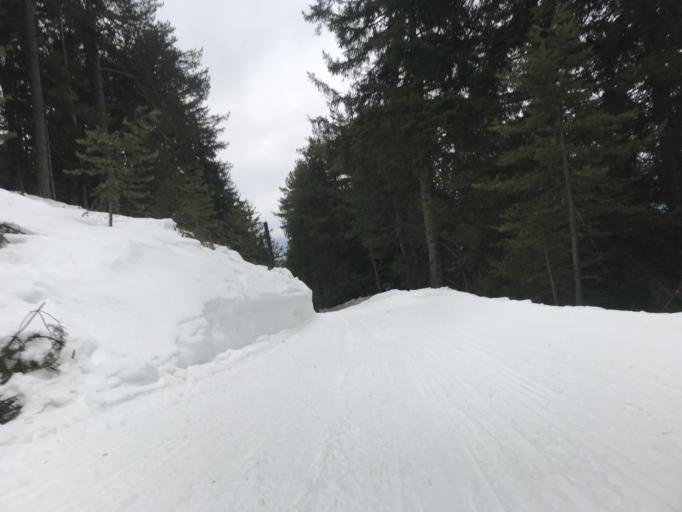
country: IT
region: Trentino-Alto Adige
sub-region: Bolzano
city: Funes - Villnoess
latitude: 46.6820
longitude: 11.6882
